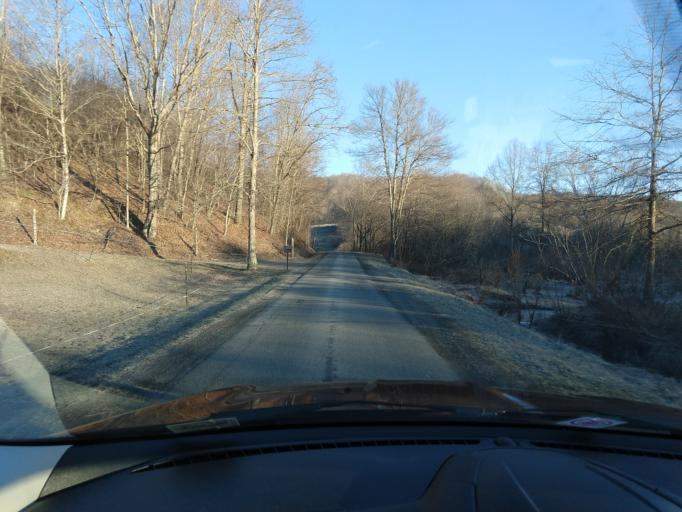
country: US
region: West Virginia
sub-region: Greenbrier County
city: Rainelle
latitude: 37.8986
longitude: -80.7322
